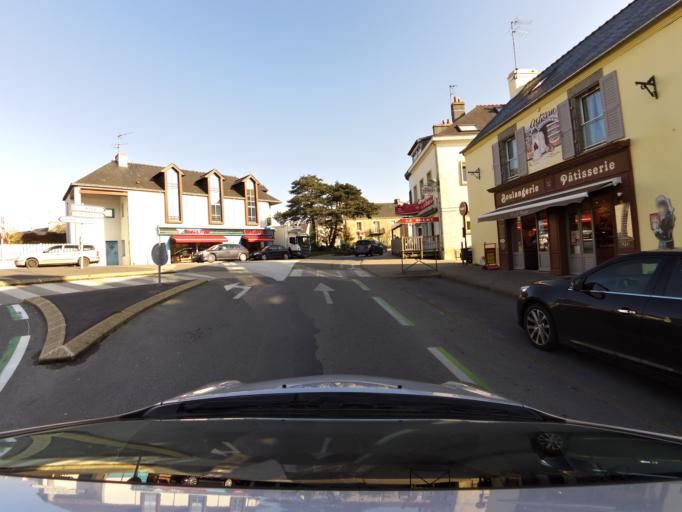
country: FR
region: Brittany
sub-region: Departement du Morbihan
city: Guidel-Plage
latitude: 47.7886
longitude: -3.4891
